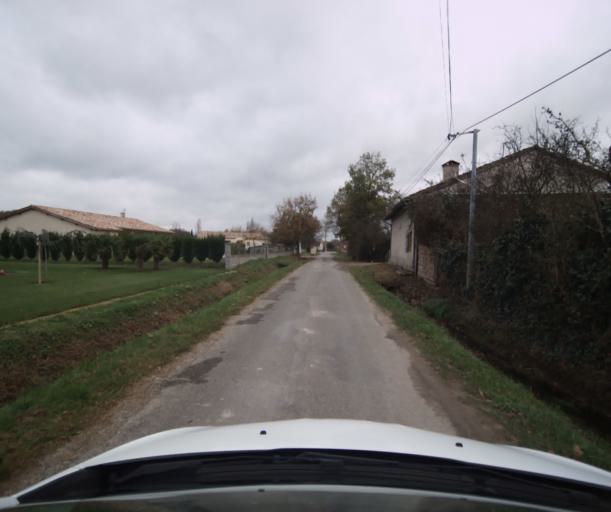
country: FR
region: Midi-Pyrenees
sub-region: Departement du Tarn-et-Garonne
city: Saint-Porquier
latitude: 44.0539
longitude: 1.1746
